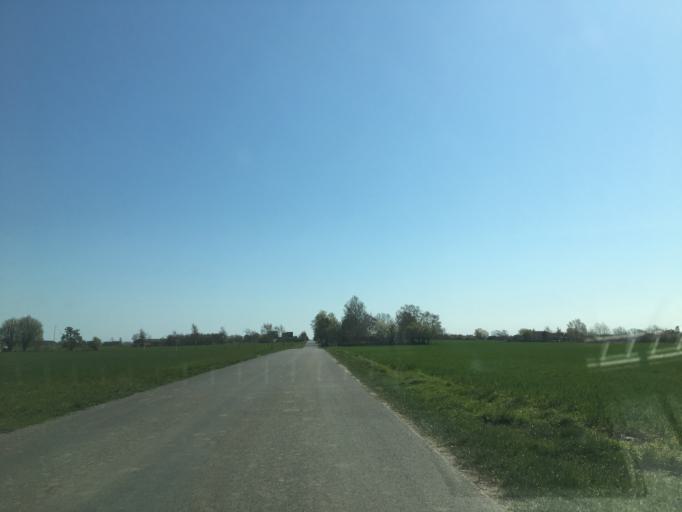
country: DK
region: Zealand
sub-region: Guldborgsund Kommune
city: Nykobing Falster
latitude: 54.7438
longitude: 11.7840
